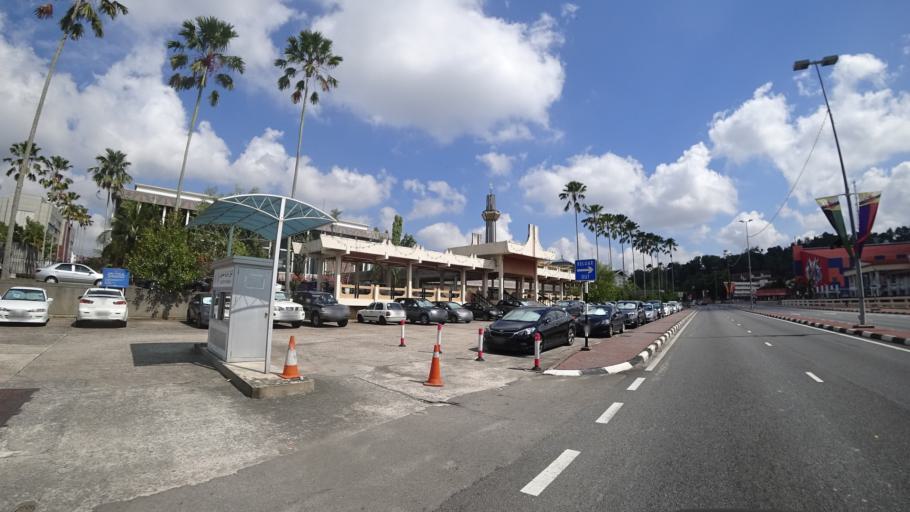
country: BN
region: Brunei and Muara
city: Bandar Seri Begawan
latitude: 4.8914
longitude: 114.9437
